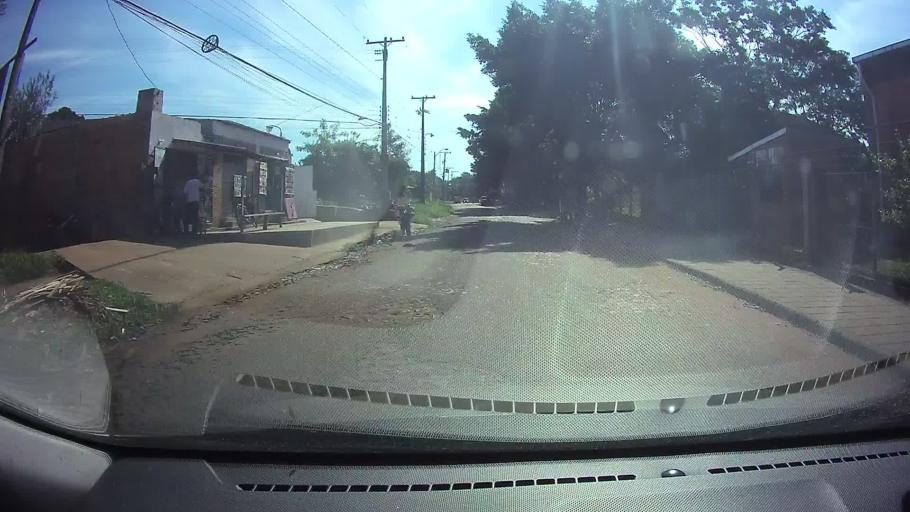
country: PY
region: Central
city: Villa Elisa
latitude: -25.3639
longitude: -57.5690
